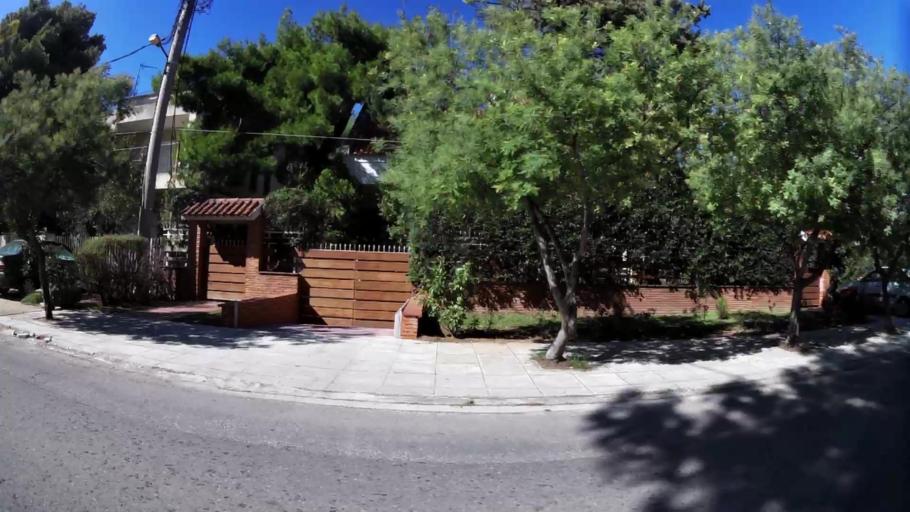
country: GR
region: Attica
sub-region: Nomarchia Athinas
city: Nea Erythraia
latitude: 38.0909
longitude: 23.8030
